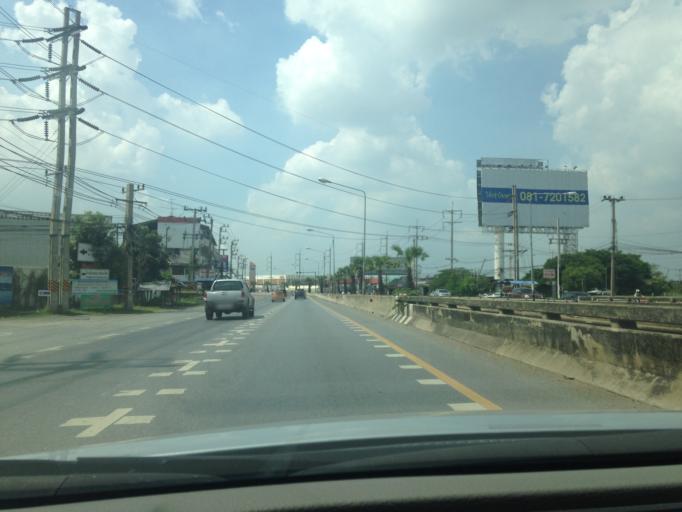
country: TH
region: Phra Nakhon Si Ayutthaya
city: Ban Bang Kadi Pathum Thani
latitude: 14.0043
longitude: 100.5655
